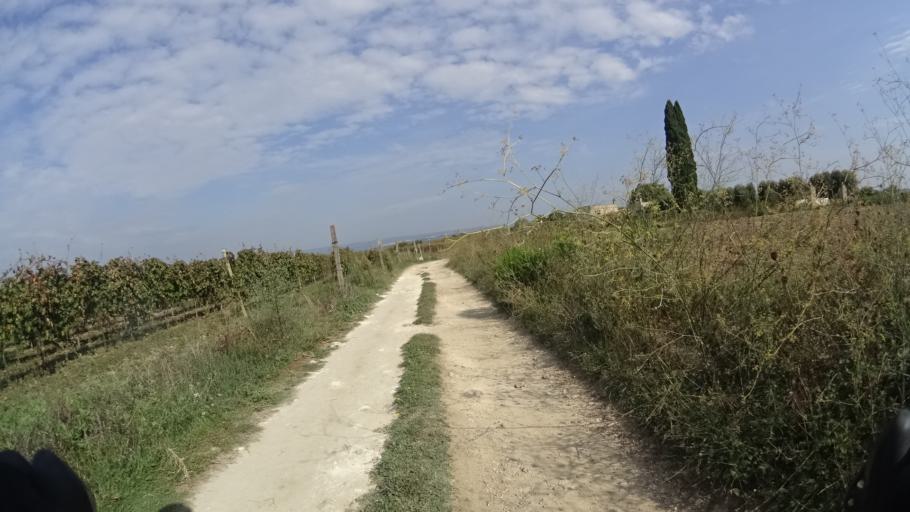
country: IT
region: Apulia
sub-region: Provincia di Taranto
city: Fragagnano
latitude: 40.4634
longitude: 17.4658
